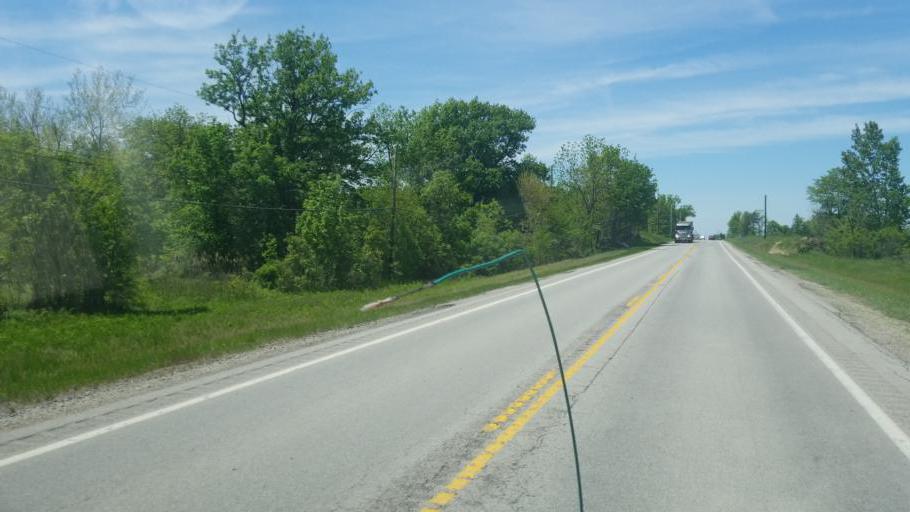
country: US
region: Ohio
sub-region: Huron County
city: Norwalk
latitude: 41.1947
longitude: -82.5749
